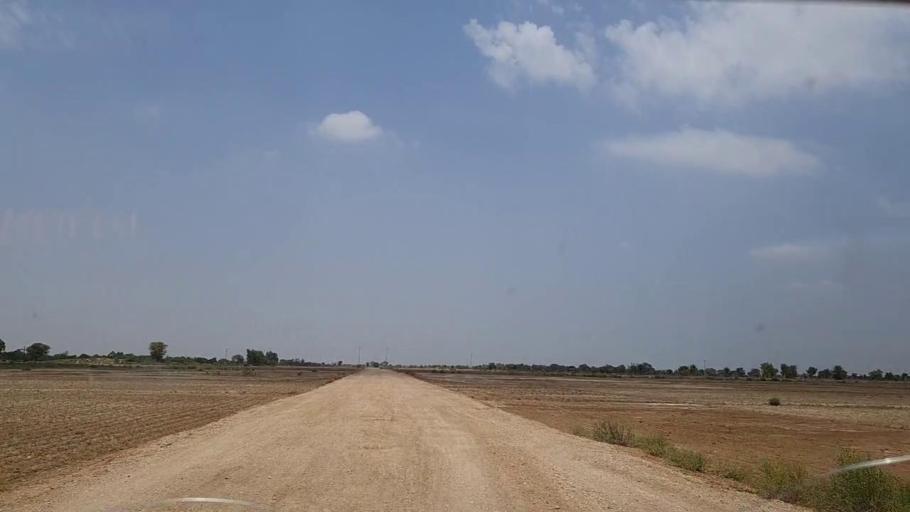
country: PK
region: Sindh
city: Phulji
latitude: 26.8148
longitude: 67.6340
